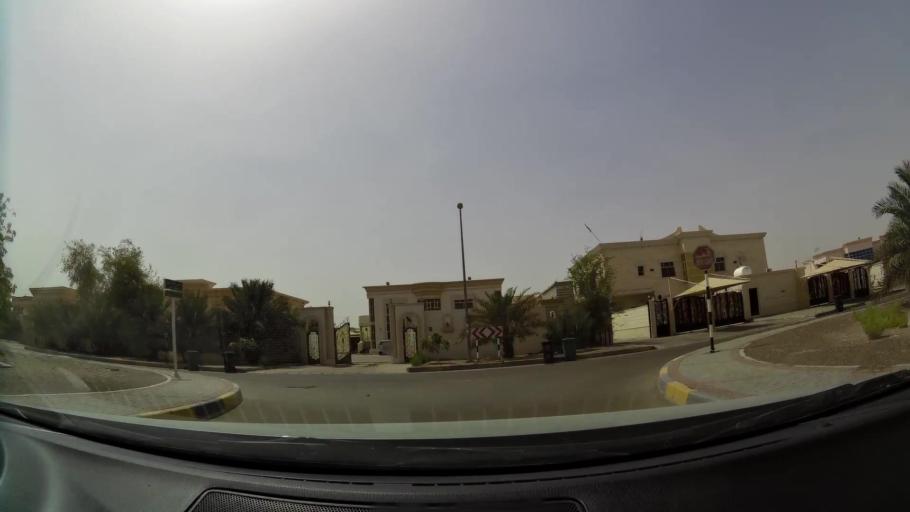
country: AE
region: Abu Dhabi
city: Al Ain
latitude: 24.1612
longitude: 55.6573
